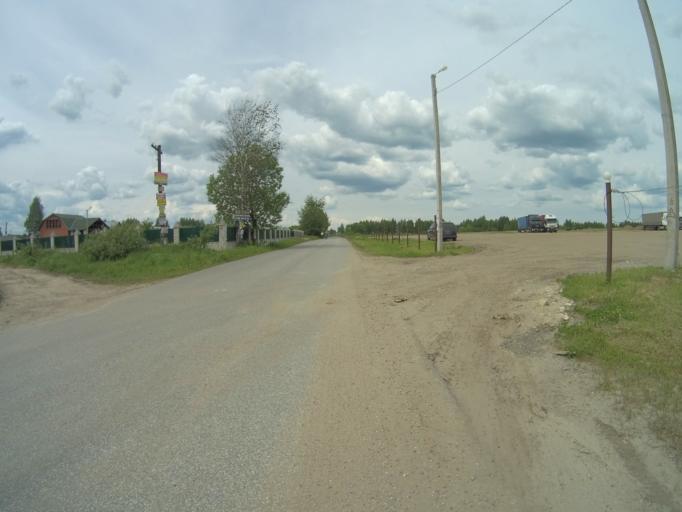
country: RU
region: Vladimir
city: Vorsha
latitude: 56.0692
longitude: 40.1527
